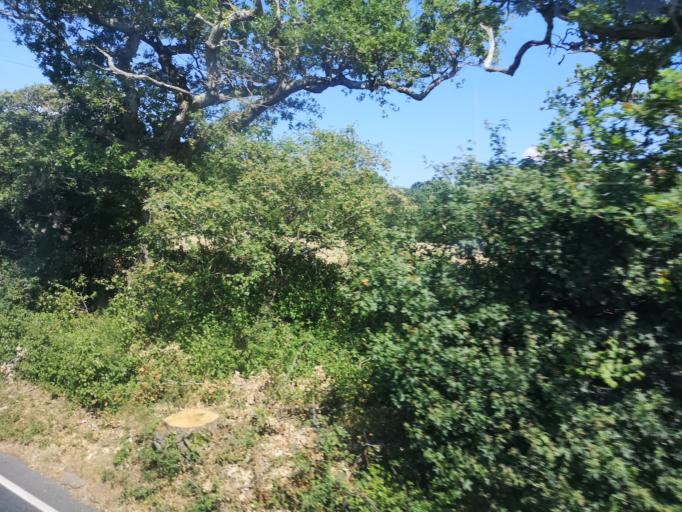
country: GB
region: England
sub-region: Isle of Wight
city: Shalfleet
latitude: 50.7027
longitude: -1.3759
